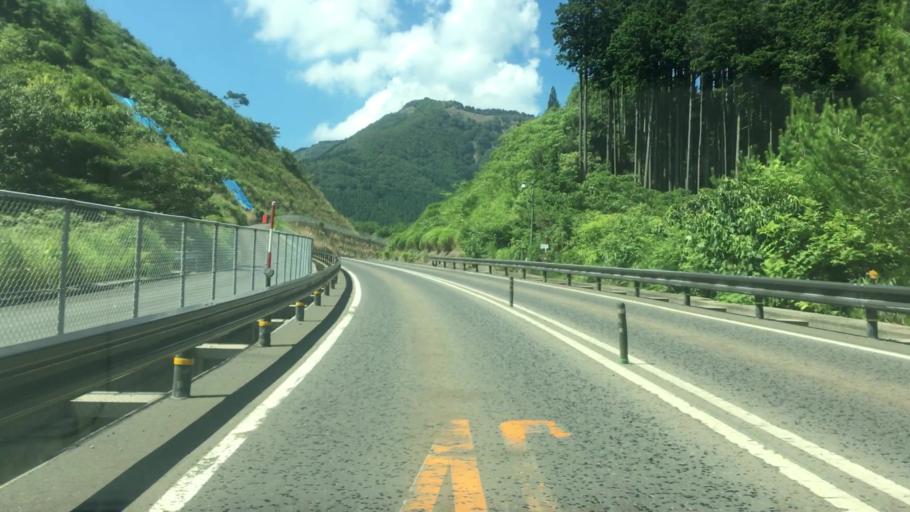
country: JP
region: Tottori
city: Tottori
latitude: 35.2826
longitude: 134.2266
